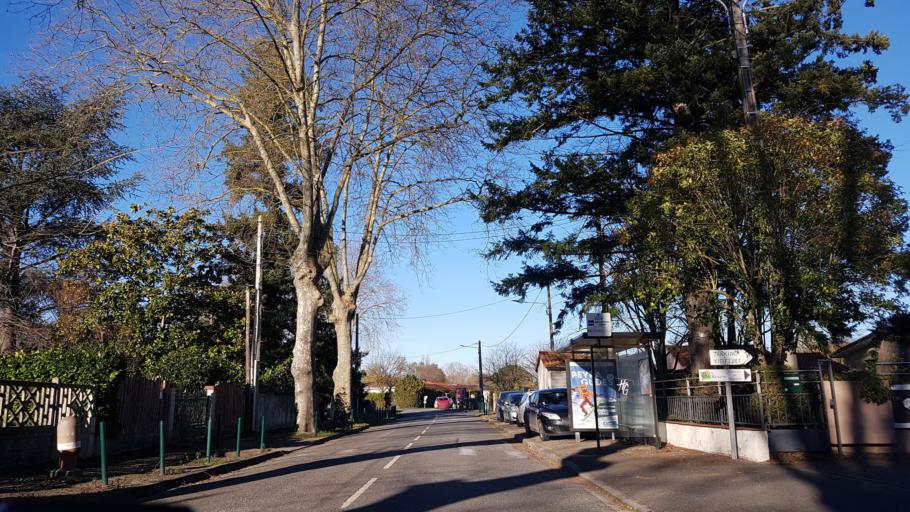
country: FR
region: Midi-Pyrenees
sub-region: Departement de la Haute-Garonne
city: Calmont
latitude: 43.2873
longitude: 1.6260
